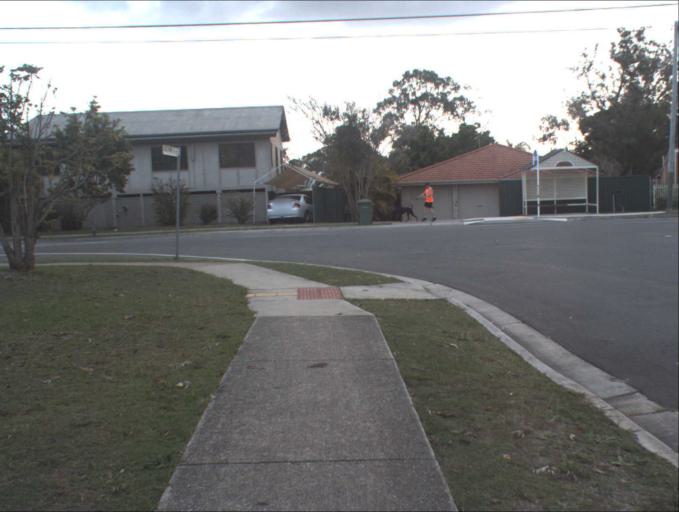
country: AU
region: Queensland
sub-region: Logan
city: Waterford West
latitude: -27.6815
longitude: 153.1325
